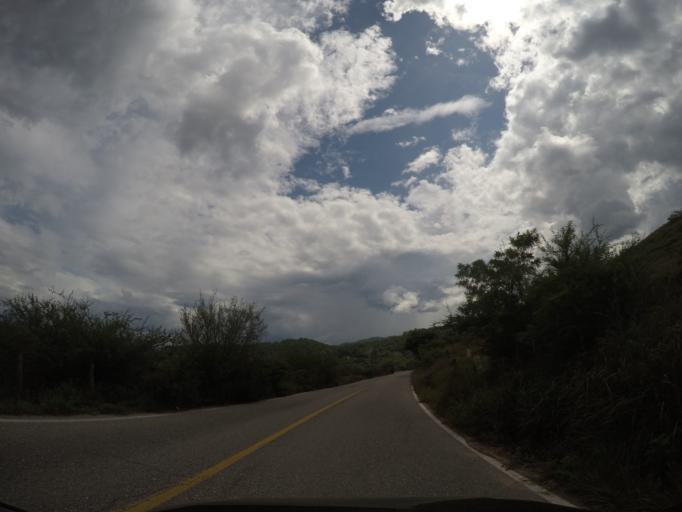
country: MX
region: Oaxaca
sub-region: San Jeronimo Coatlan
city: San Cristobal Honduras
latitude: 16.4284
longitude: -97.0689
